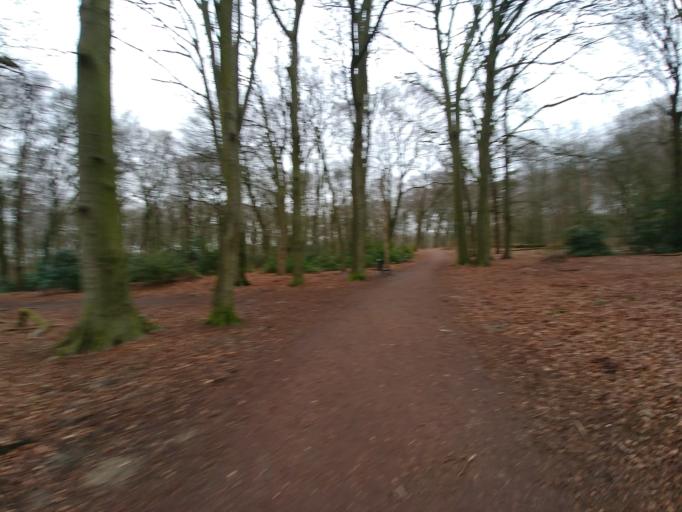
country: NL
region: South Holland
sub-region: Gemeente Leidschendam-Voorburg
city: Voorburg
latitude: 52.1041
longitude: 4.3347
